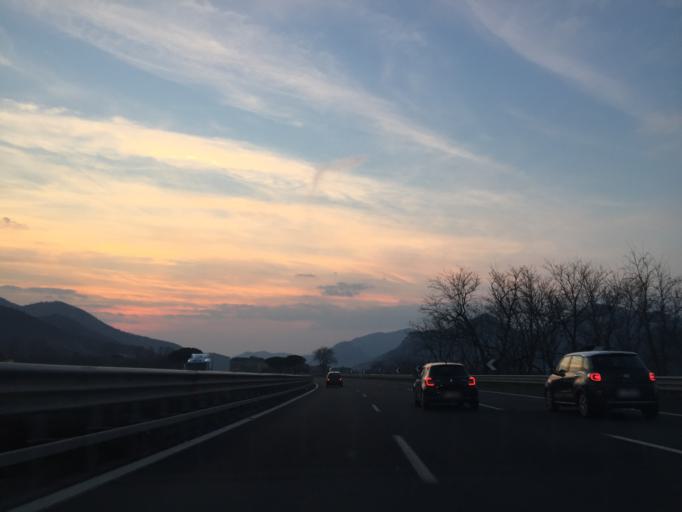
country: IT
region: Campania
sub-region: Provincia di Salerno
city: Faraldo-Nocelleto
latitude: 40.7742
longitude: 14.7634
